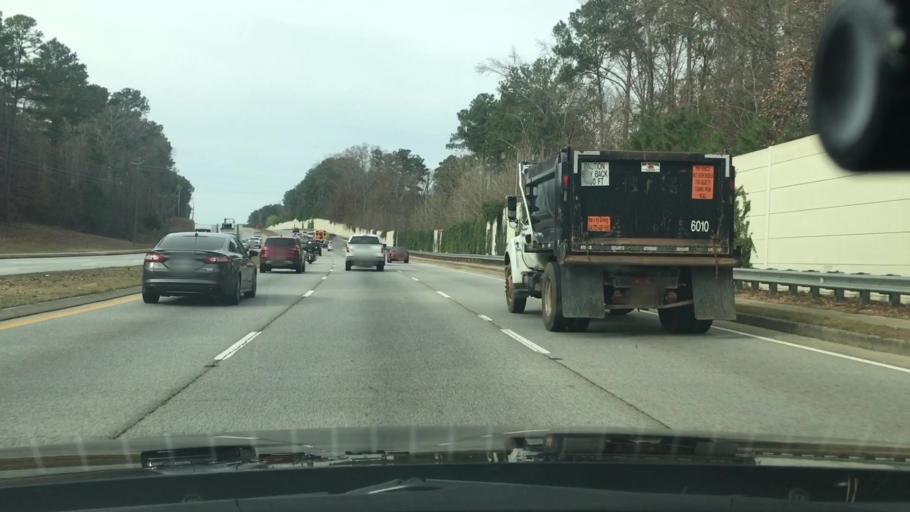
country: US
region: Georgia
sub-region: Fayette County
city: Peachtree City
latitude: 33.3848
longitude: -84.5786
